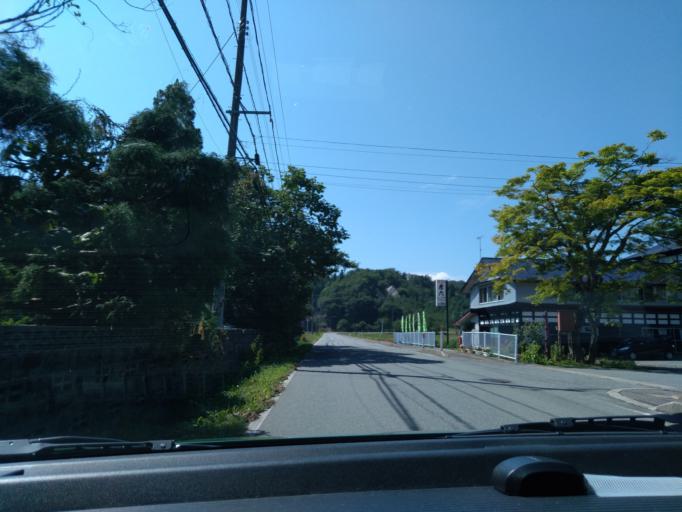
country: JP
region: Akita
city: Kakunodatemachi
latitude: 39.7326
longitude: 140.7086
